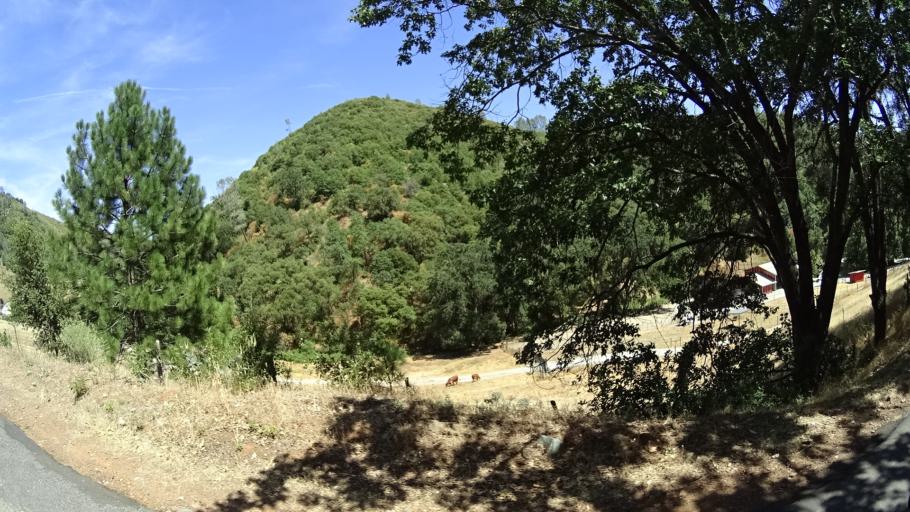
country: US
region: California
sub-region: Calaveras County
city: Murphys
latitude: 38.1645
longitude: -120.4740
